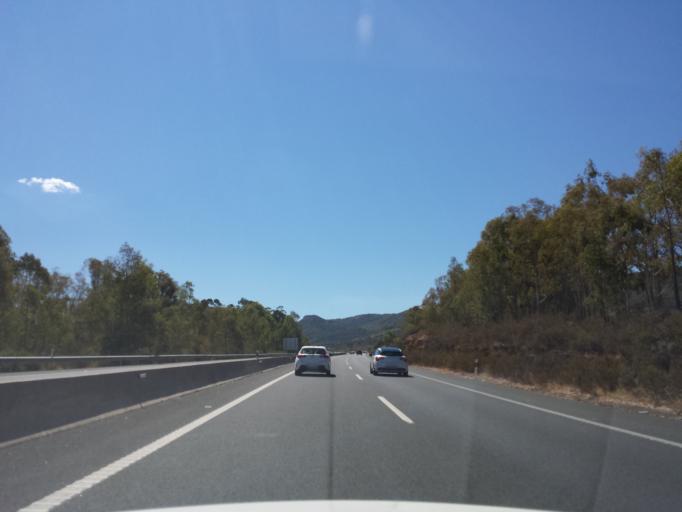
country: ES
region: Extremadura
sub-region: Provincia de Caceres
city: Romangordo
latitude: 39.7226
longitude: -5.7123
